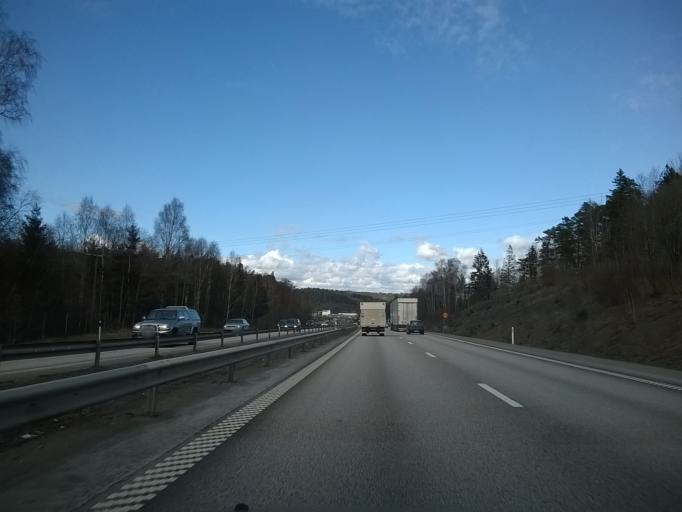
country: SE
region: Halland
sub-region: Kungsbacka Kommun
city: Kungsbacka
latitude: 57.4959
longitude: 12.0501
